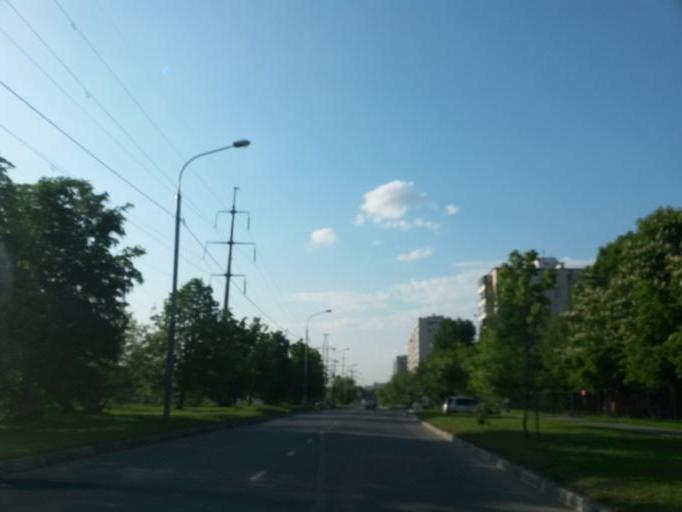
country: RU
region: Moskovskaya
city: Biryulevo Zapadnoye
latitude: 55.5845
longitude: 37.6409
